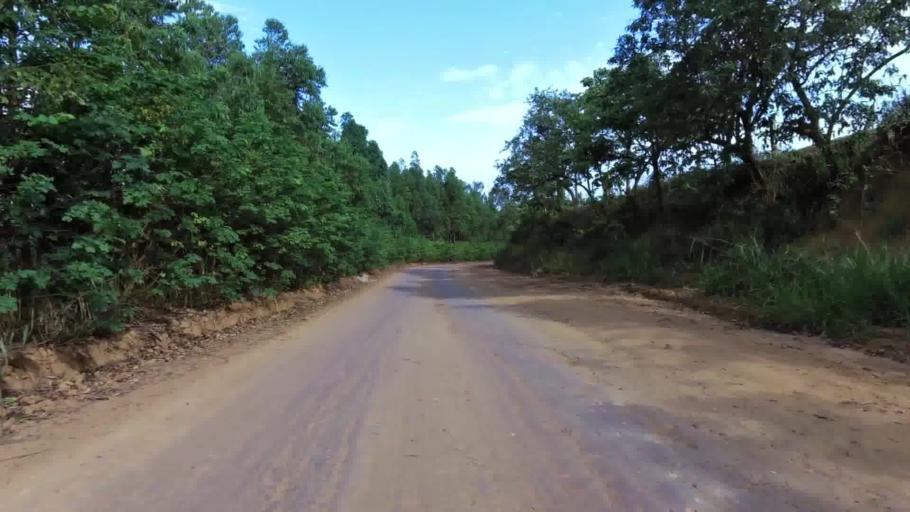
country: BR
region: Espirito Santo
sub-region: Piuma
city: Piuma
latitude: -20.8301
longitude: -40.7405
